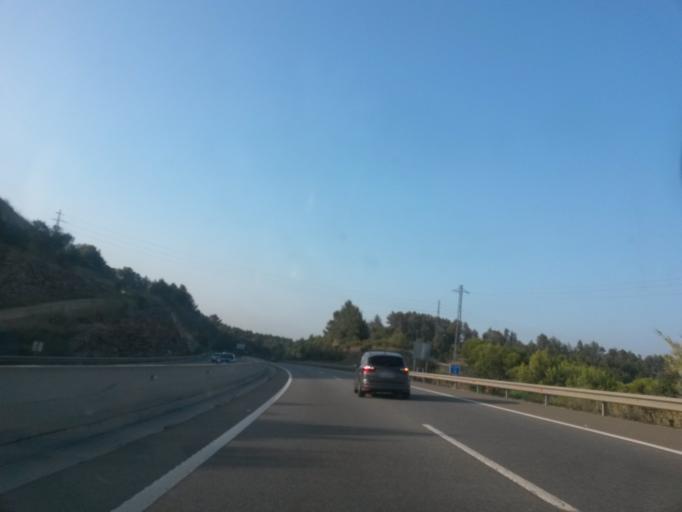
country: ES
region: Catalonia
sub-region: Provincia de Barcelona
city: Palleja
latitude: 41.4081
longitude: 1.9896
